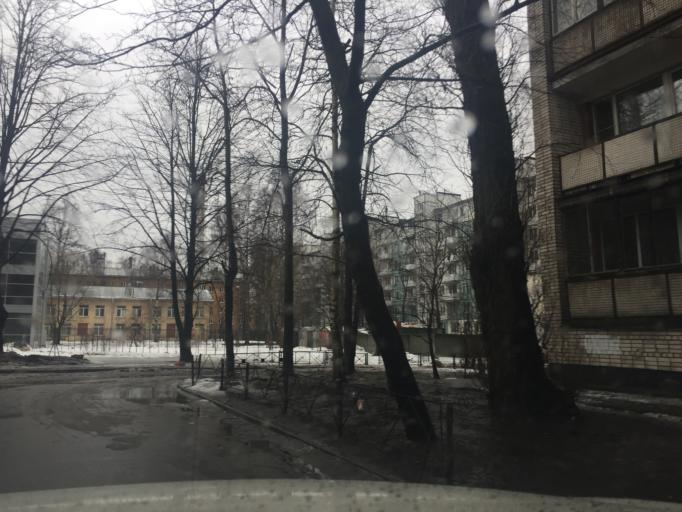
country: RU
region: Leningrad
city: Kalininskiy
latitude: 59.9541
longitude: 30.4204
